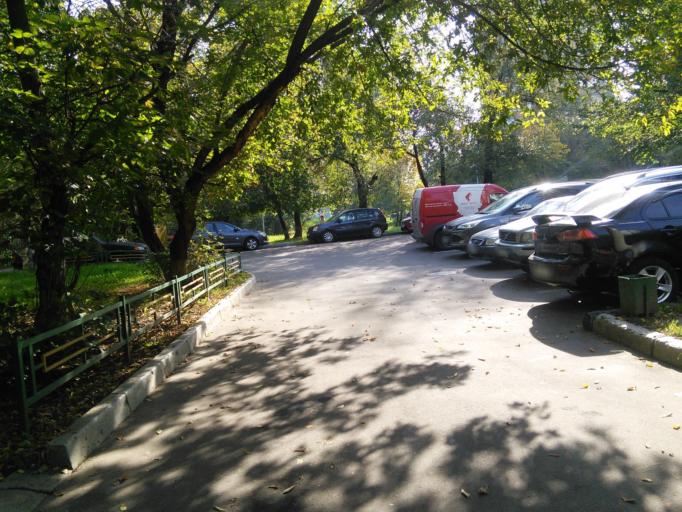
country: RU
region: Moscow
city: Tsaritsyno
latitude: 55.6362
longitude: 37.6586
